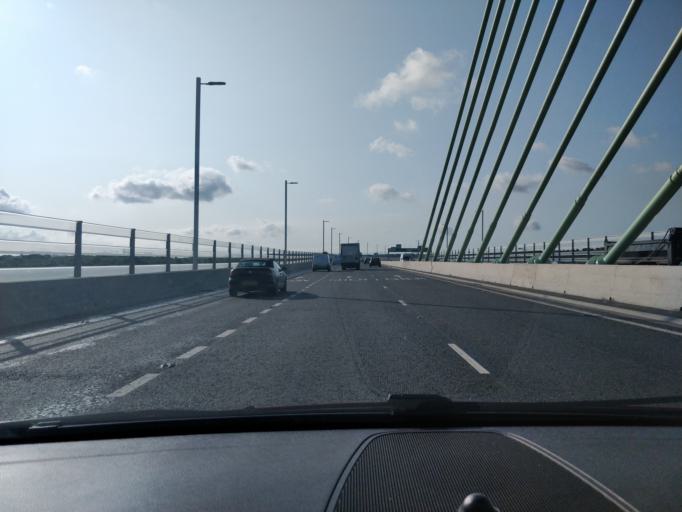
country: GB
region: England
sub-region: Borough of Halton
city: Runcorn
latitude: 53.3502
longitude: -2.7079
